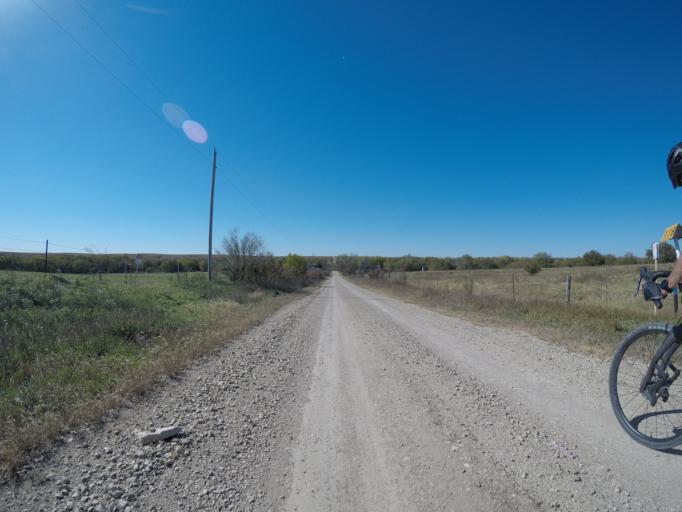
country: US
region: Kansas
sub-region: Wabaunsee County
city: Alma
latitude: 39.0290
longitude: -96.3852
